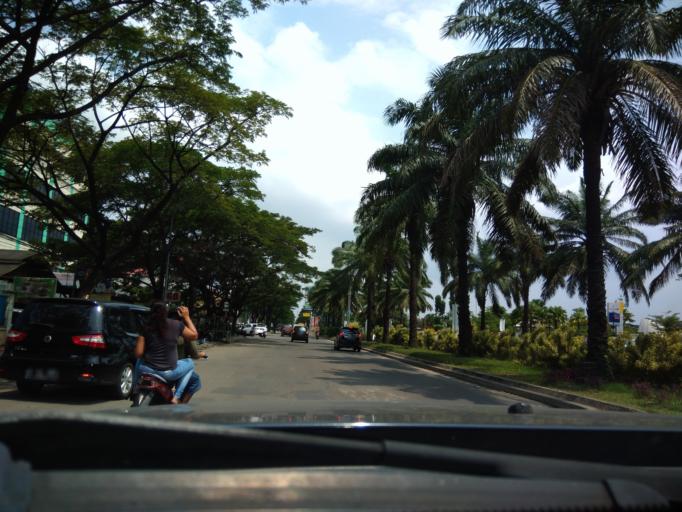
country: ID
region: West Java
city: Bekasi
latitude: -6.1846
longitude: 106.9772
